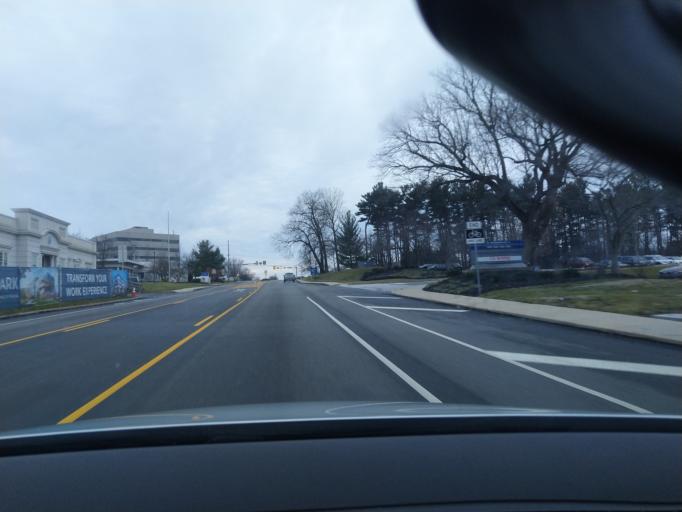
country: US
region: Pennsylvania
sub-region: Montgomery County
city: King of Prussia
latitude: 40.0951
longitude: -75.4085
